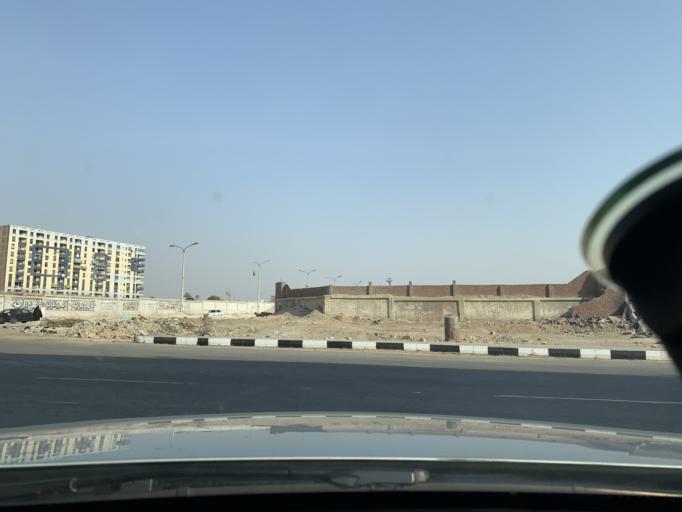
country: EG
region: Muhafazat al Qalyubiyah
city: Al Khankah
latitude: 30.1351
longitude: 31.3852
